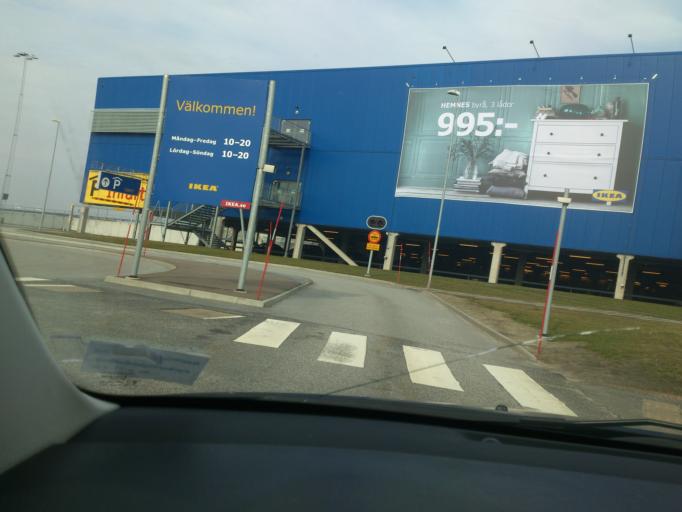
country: SE
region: Skane
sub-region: Malmo
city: Tygelsjo
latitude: 55.5512
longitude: 12.9864
